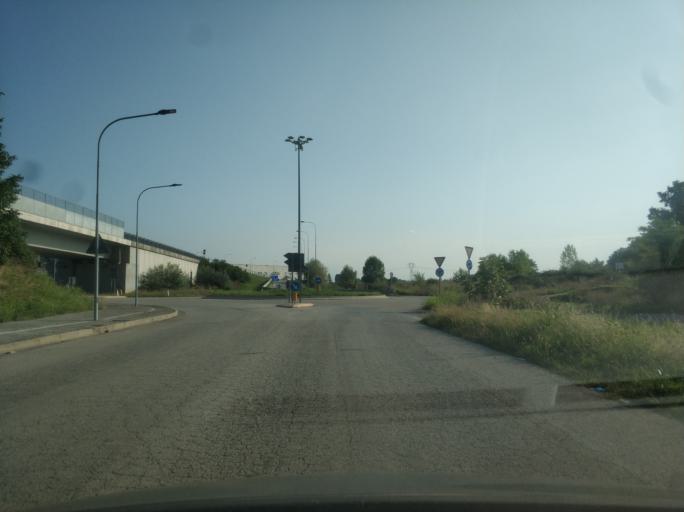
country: IT
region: Piedmont
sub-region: Provincia di Cuneo
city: Roreto
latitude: 44.6670
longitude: 7.8231
